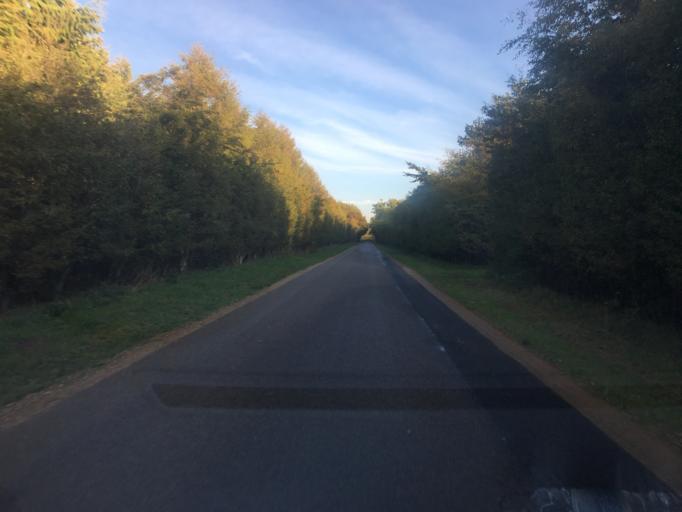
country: DE
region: Schleswig-Holstein
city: Ellhoft
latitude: 54.9143
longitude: 8.9850
